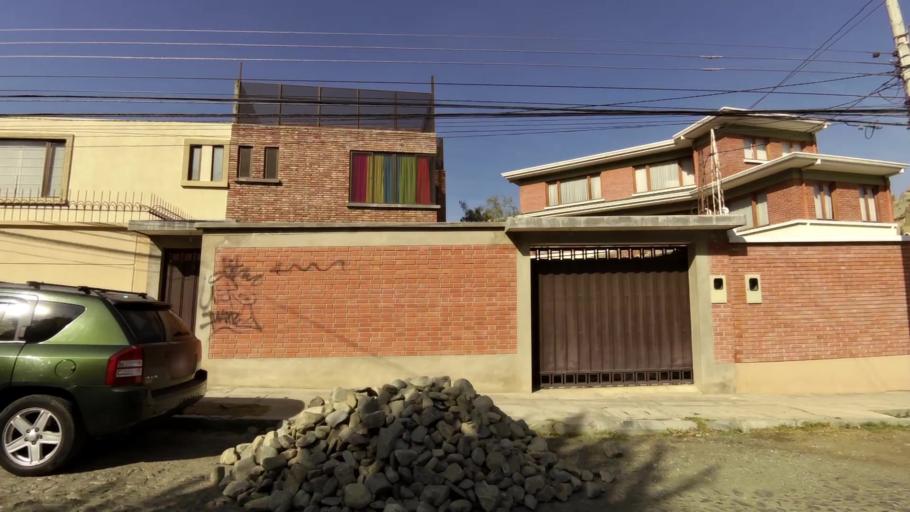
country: BO
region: La Paz
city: La Paz
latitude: -16.5218
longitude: -68.0655
